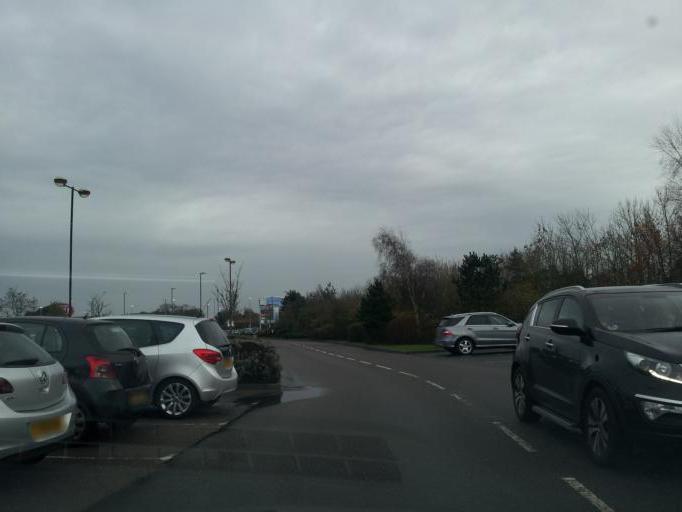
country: GB
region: England
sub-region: Norfolk
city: Costessey
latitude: 52.6531
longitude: 1.1804
